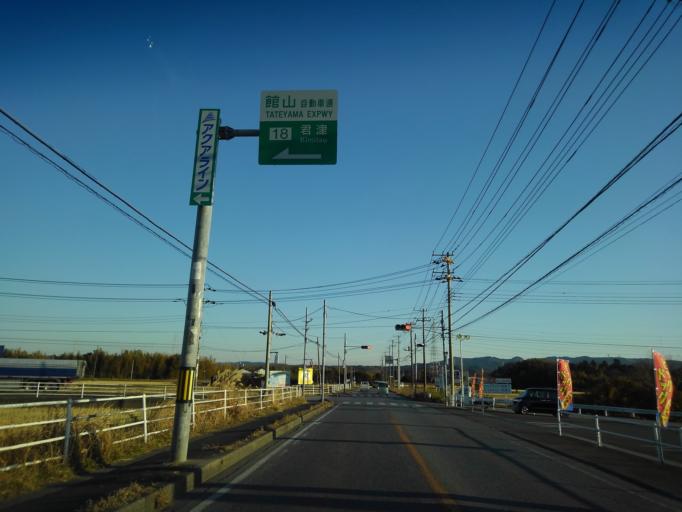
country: JP
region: Chiba
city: Kimitsu
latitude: 35.3142
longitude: 139.9340
